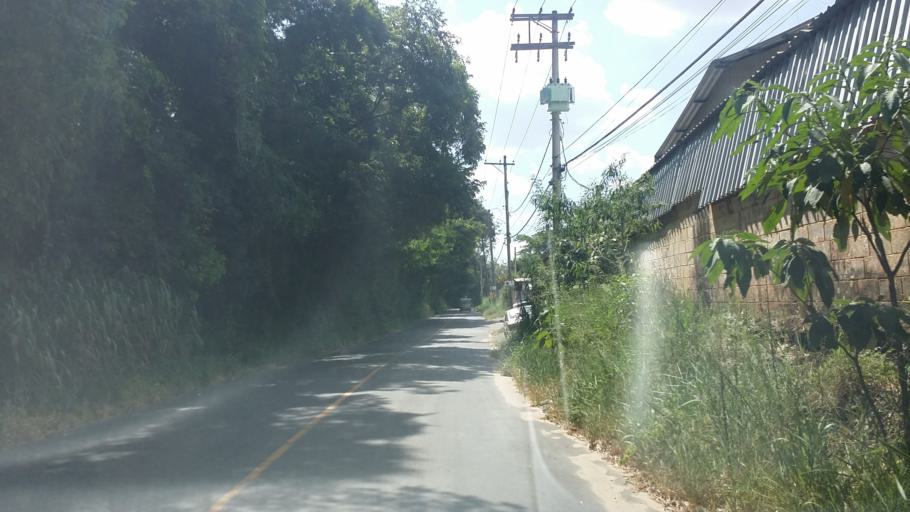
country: BR
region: Sao Paulo
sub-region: Itupeva
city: Itupeva
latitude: -23.1938
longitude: -47.0247
